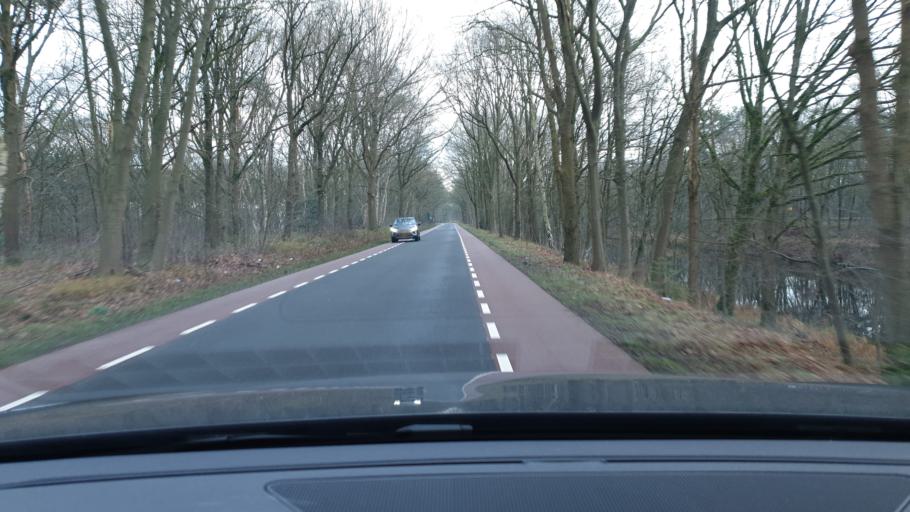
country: NL
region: North Brabant
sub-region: Gemeente Best
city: Best
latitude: 51.5039
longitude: 5.4393
